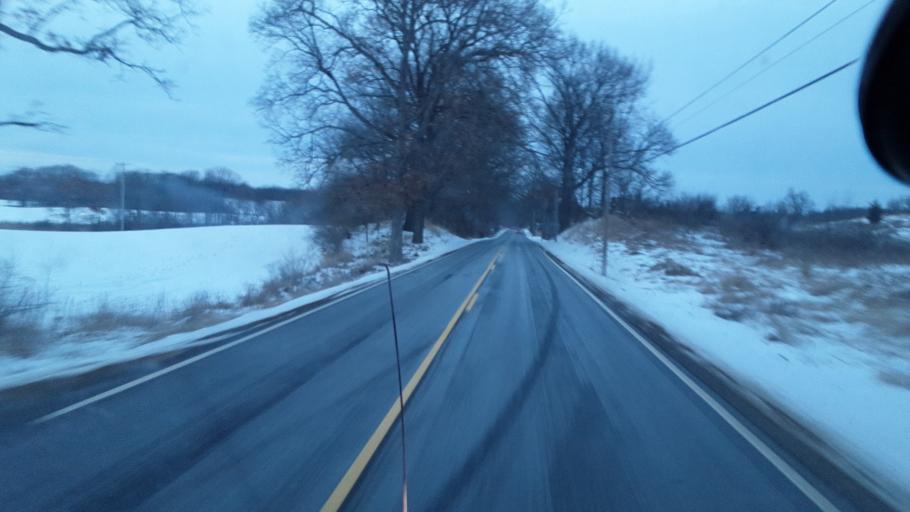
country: US
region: Michigan
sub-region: Jackson County
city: Grass Lake
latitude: 42.3139
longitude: -84.2096
